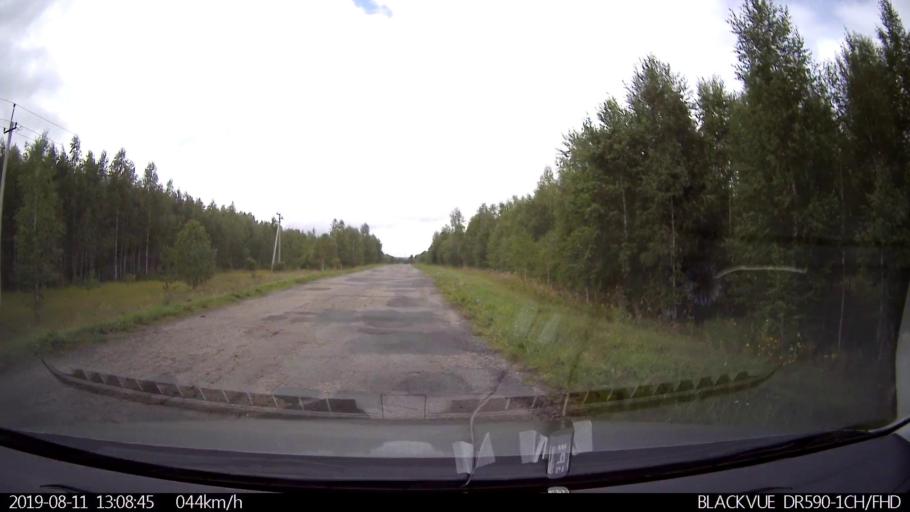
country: RU
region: Ulyanovsk
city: Ignatovka
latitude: 53.8591
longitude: 47.6299
